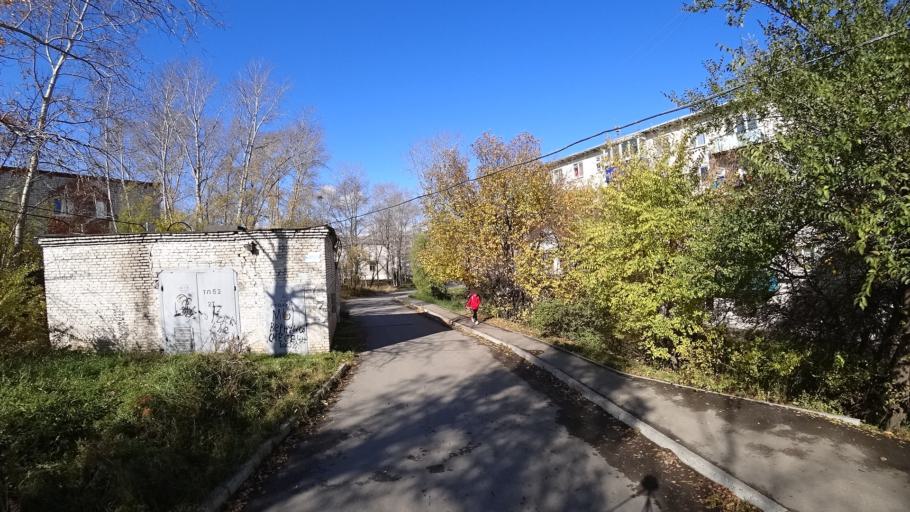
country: RU
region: Khabarovsk Krai
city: Amursk
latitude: 50.2218
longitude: 136.9088
